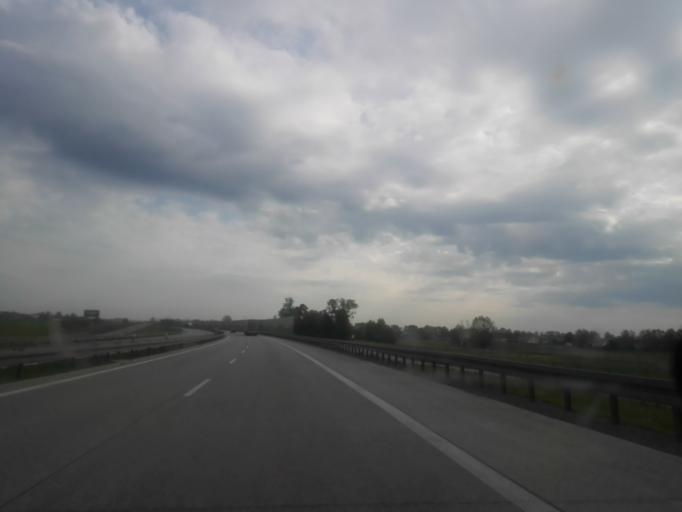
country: PL
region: Lodz Voivodeship
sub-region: Powiat tomaszowski
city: Lubochnia
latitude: 51.5954
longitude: 20.0533
